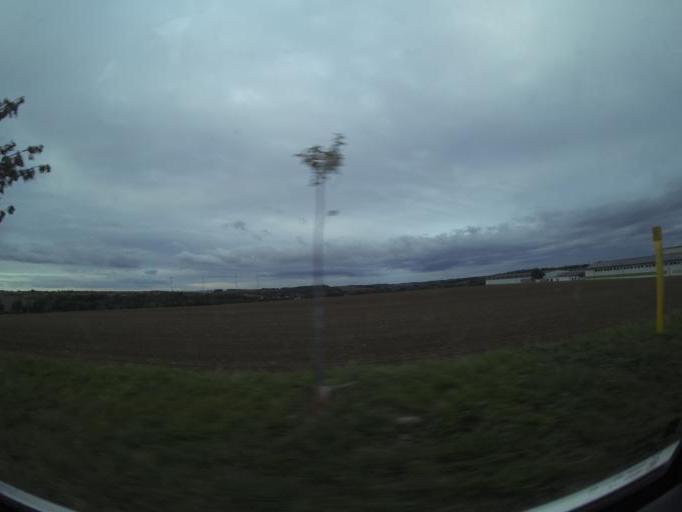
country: DE
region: Thuringia
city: Nobdenitz
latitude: 50.8819
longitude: 12.2776
